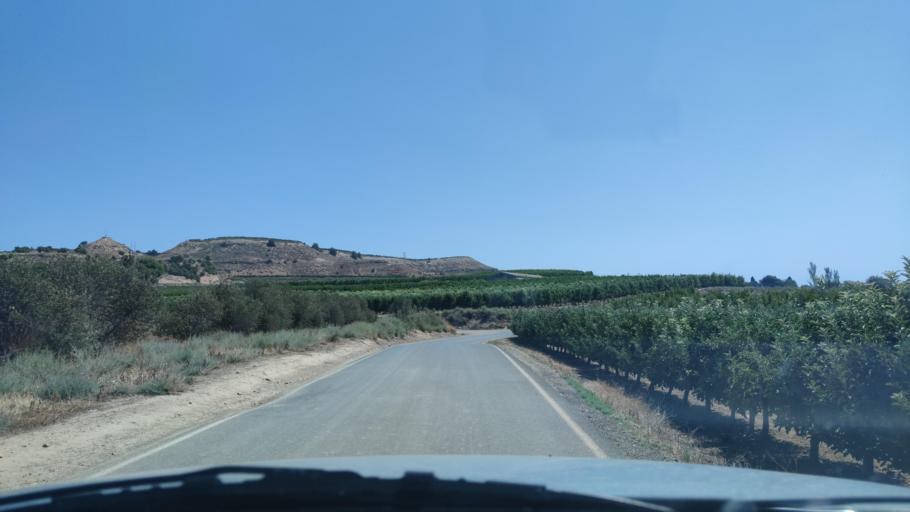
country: ES
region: Catalonia
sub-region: Provincia de Lleida
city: Alpicat
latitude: 41.6698
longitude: 0.5627
